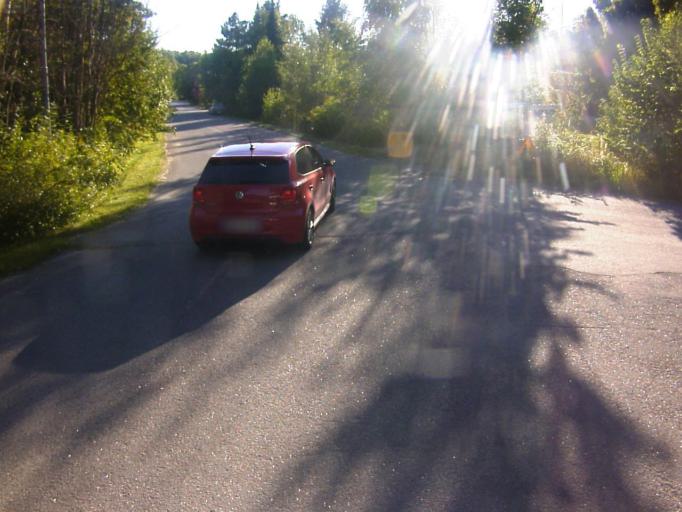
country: SE
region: Soedermanland
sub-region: Eskilstuna Kommun
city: Hallbybrunn
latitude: 59.4043
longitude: 16.4178
